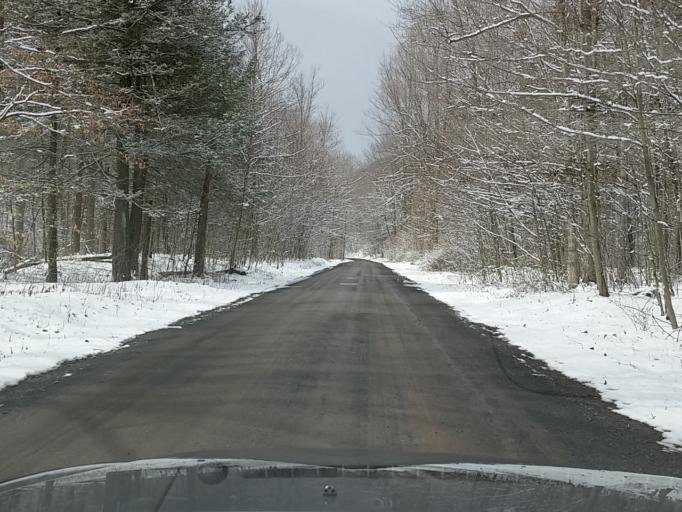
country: US
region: Pennsylvania
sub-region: Sullivan County
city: Laporte
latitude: 41.3193
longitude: -76.4467
